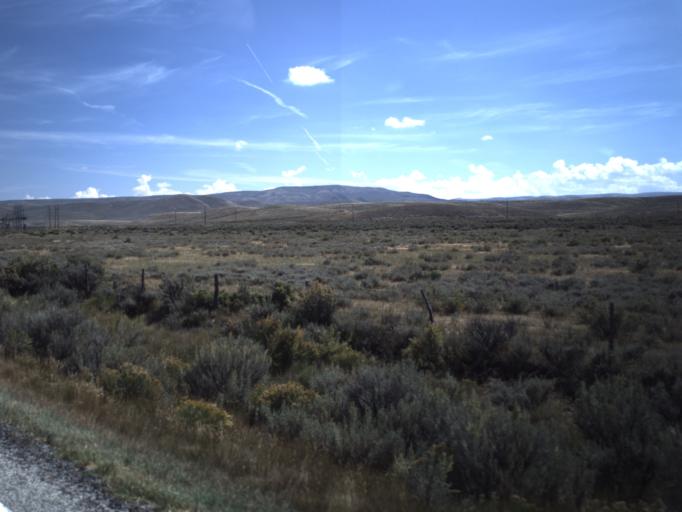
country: US
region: Utah
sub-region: Rich County
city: Randolph
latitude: 41.7790
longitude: -111.0523
